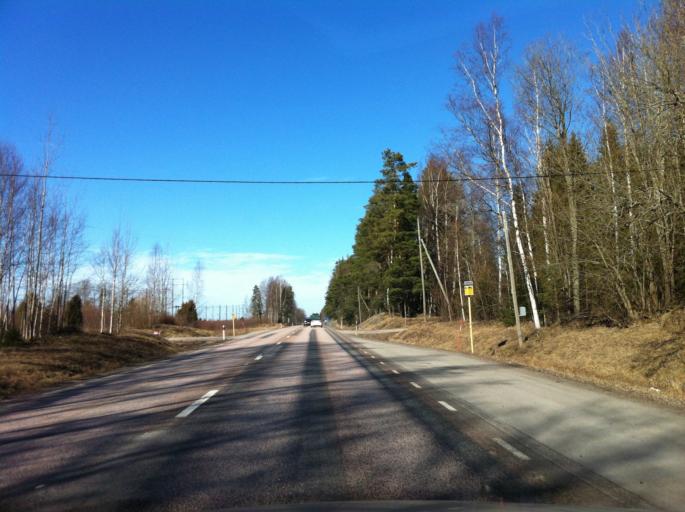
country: SE
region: Vaestra Goetaland
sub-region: Gullspangs Kommun
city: Hova
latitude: 58.9004
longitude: 14.1212
